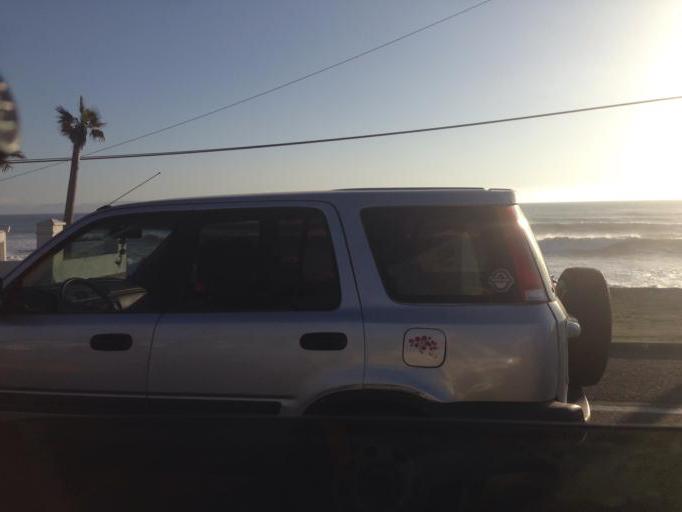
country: MX
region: Baja California
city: El Sauzal
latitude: 31.8687
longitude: -116.6742
